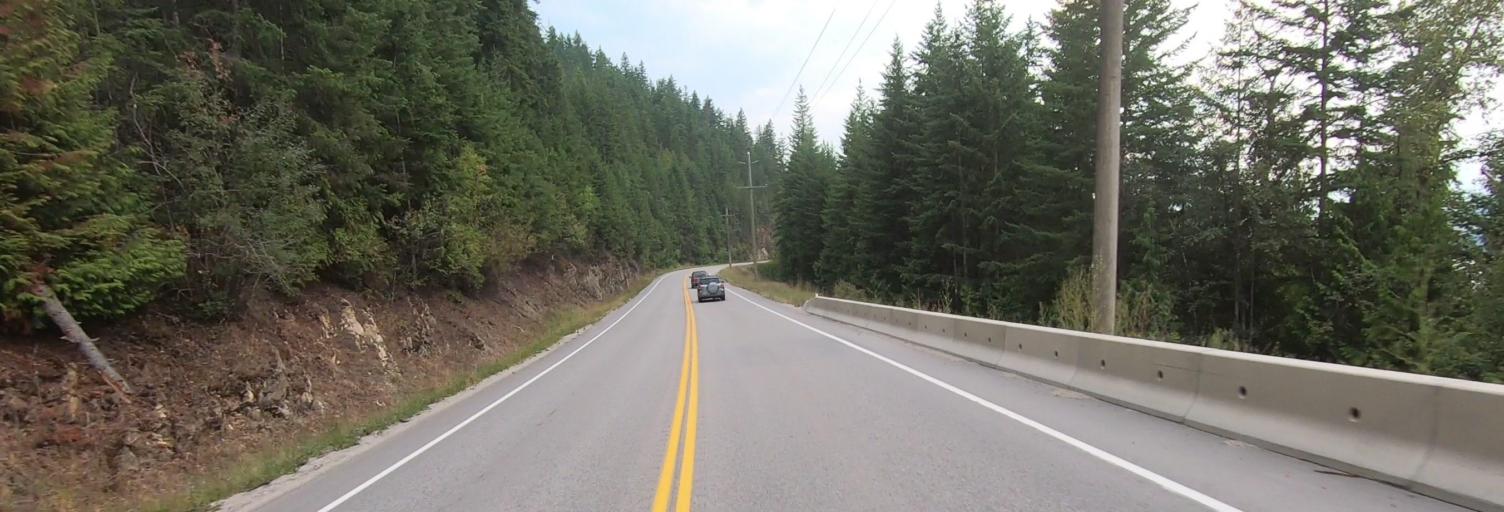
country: CA
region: British Columbia
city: Sicamous
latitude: 50.8202
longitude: -119.0365
